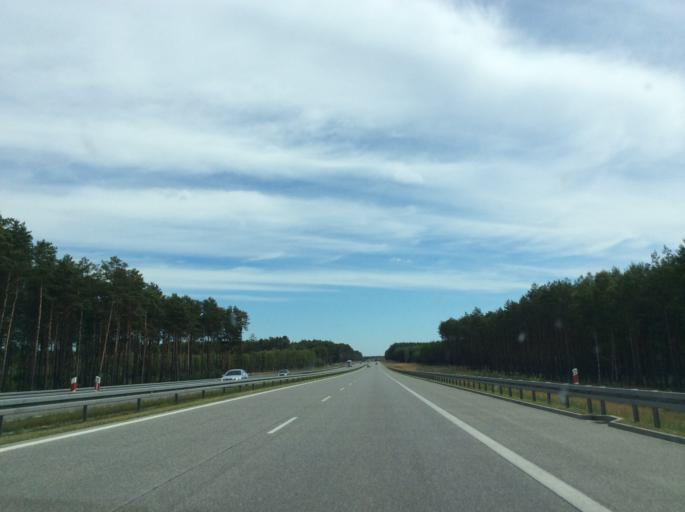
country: PL
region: Lubusz
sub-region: Powiat swiebodzinski
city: Zbaszynek
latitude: 52.3164
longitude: 15.7935
